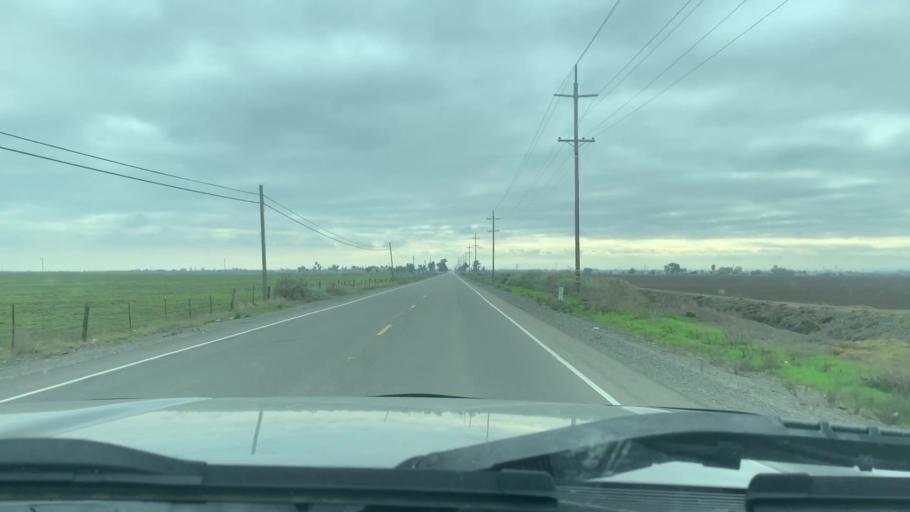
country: US
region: California
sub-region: Merced County
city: Los Banos
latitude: 37.1133
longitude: -120.8349
